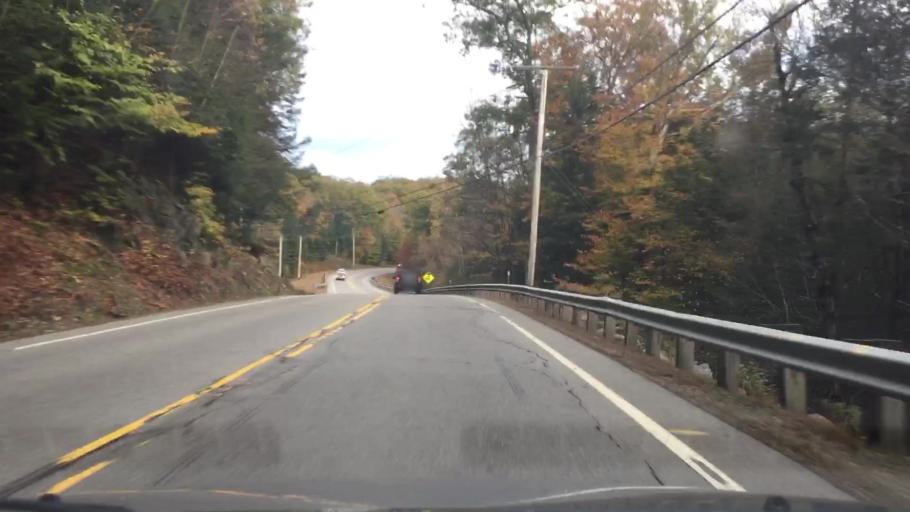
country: US
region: New Hampshire
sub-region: Cheshire County
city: Keene
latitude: 43.0209
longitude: -72.2658
